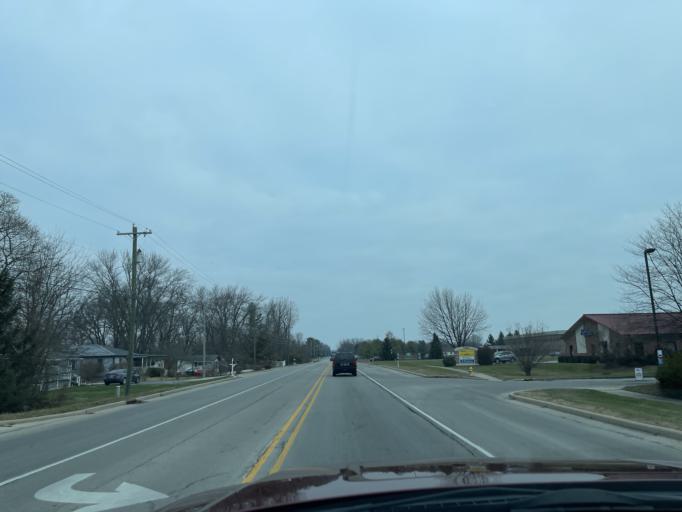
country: US
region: Indiana
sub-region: Hendricks County
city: Fairfield Heights
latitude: 39.8220
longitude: -86.4010
